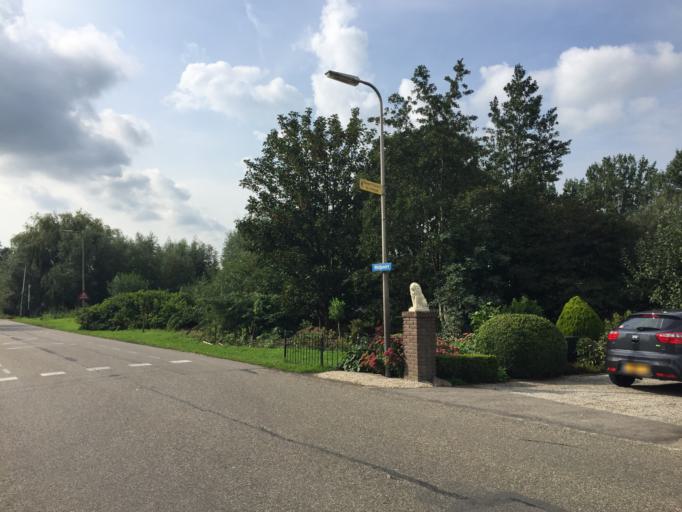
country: NL
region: South Holland
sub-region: Bodegraven-Reeuwijk
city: Bodegraven
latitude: 52.0850
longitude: 4.7904
